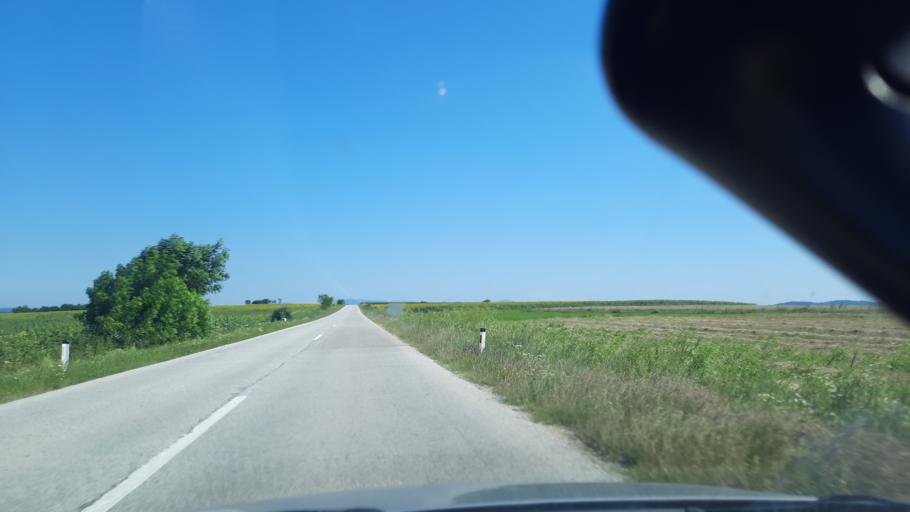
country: RS
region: Central Serbia
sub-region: Branicevski Okrug
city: Malo Crnice
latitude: 44.5679
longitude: 21.4296
